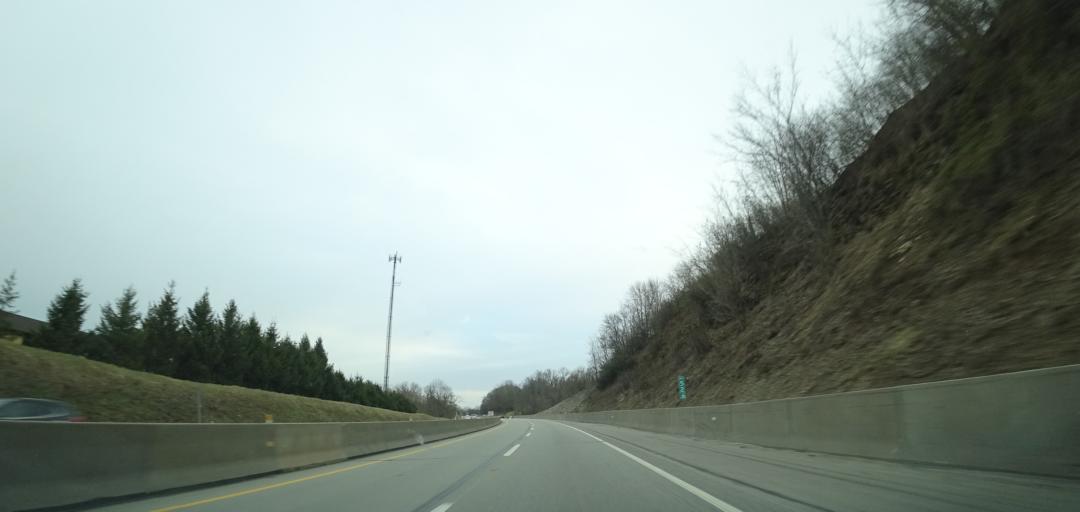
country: US
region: Pennsylvania
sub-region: Allegheny County
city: Plum
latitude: 40.4872
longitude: -79.7794
